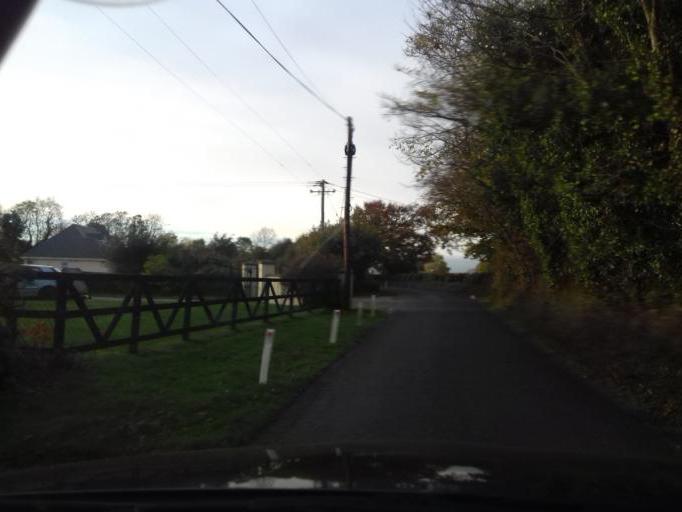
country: IE
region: Leinster
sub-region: An Mhi
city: Dunboyne
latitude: 53.3880
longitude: -6.4663
